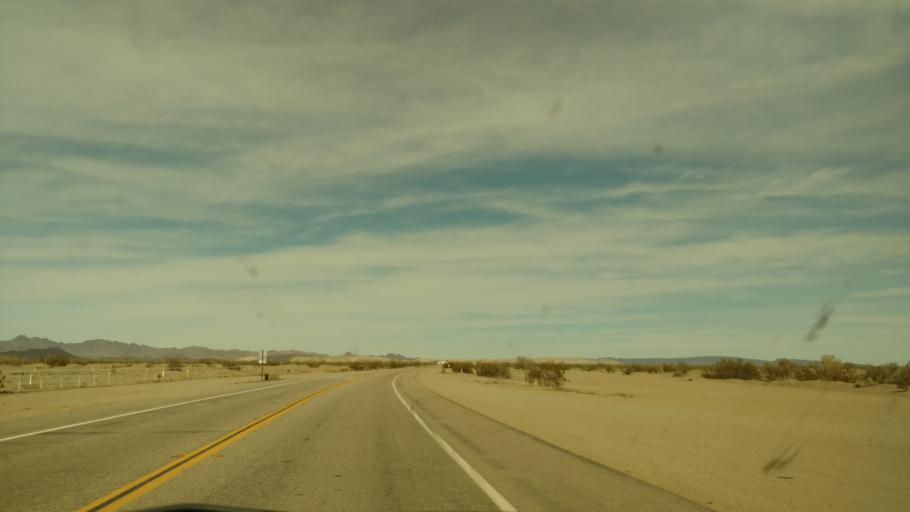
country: US
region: California
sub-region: Imperial County
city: Holtville
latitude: 32.9987
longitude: -115.0697
